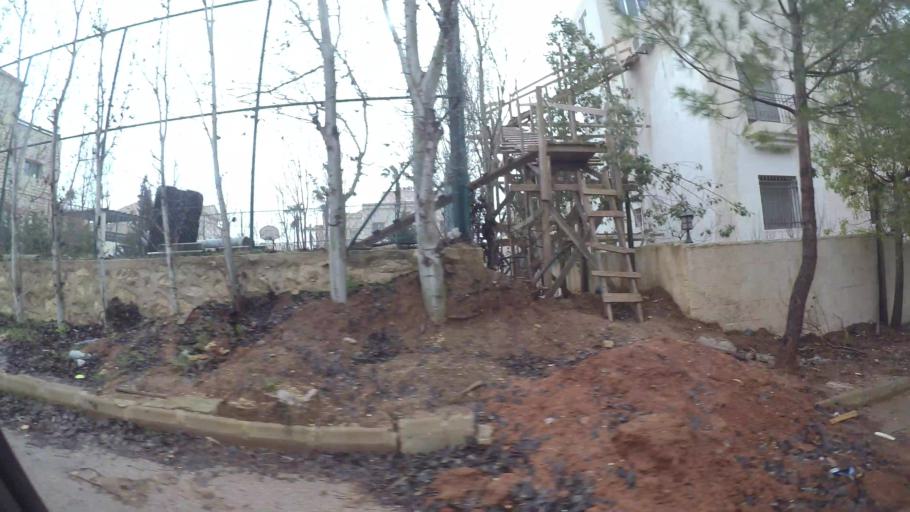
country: JO
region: Amman
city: Al Jubayhah
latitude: 32.0116
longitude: 35.8252
